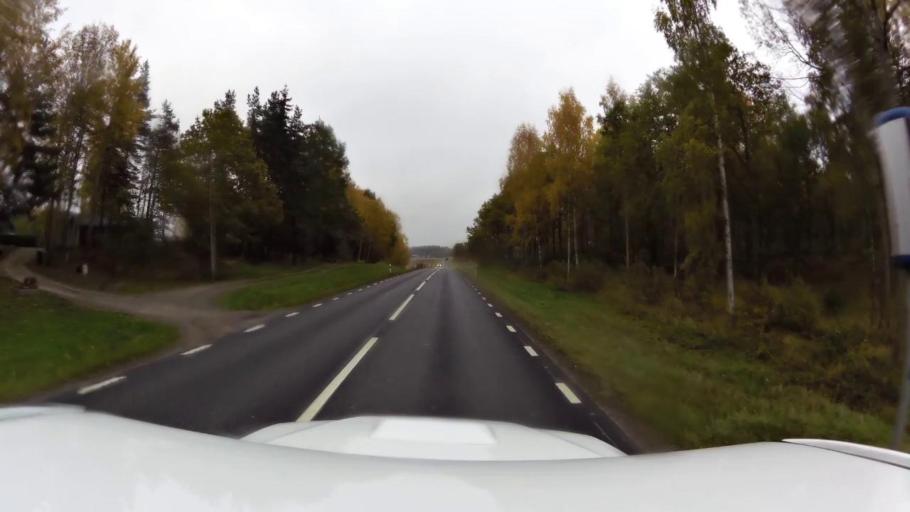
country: SE
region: OEstergoetland
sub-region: Linkopings Kommun
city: Linghem
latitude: 58.3795
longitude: 15.7987
